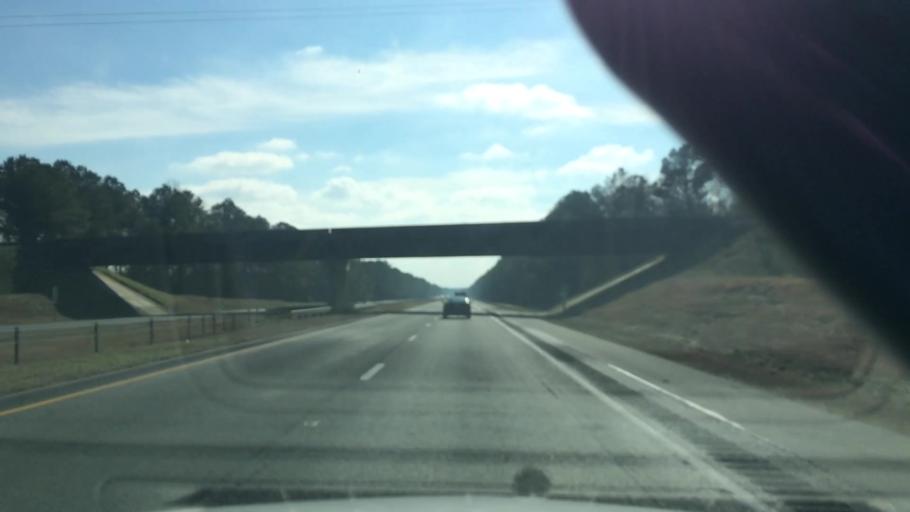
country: US
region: North Carolina
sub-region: Duplin County
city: Wallace
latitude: 34.7326
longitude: -77.9449
